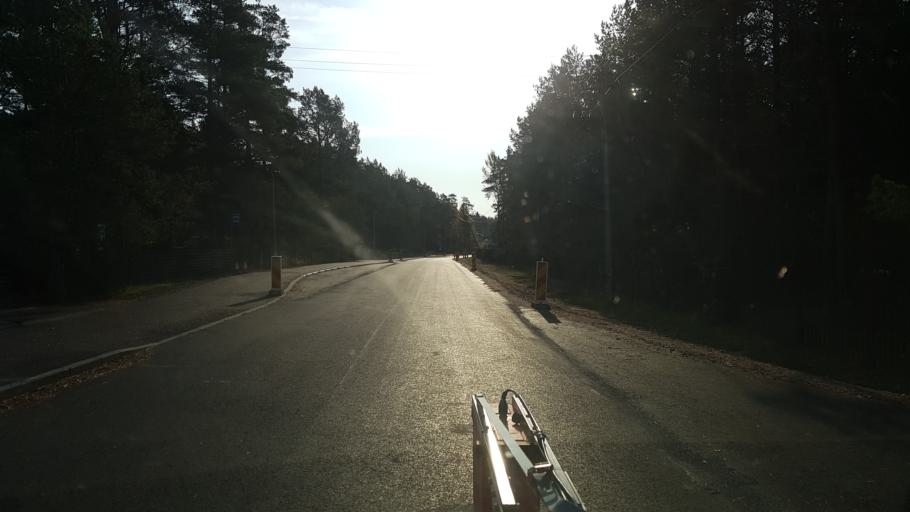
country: EE
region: Paernumaa
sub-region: Paikuse vald
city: Paikuse
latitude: 58.3555
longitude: 24.6167
